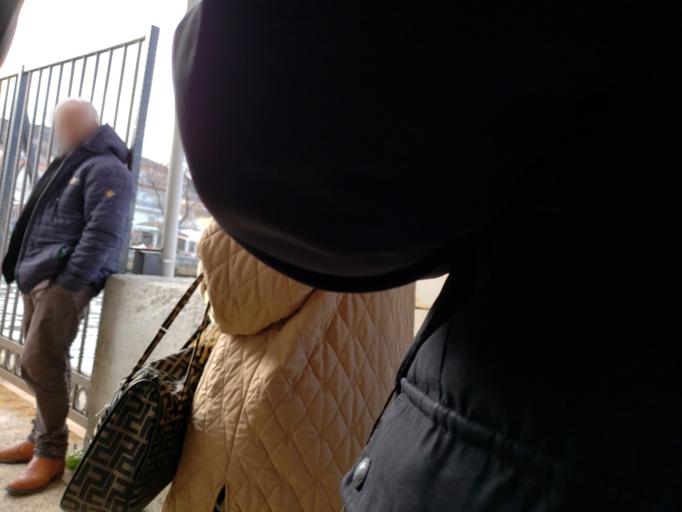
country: TR
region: Istanbul
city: Adalan
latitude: 40.8771
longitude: 29.1019
